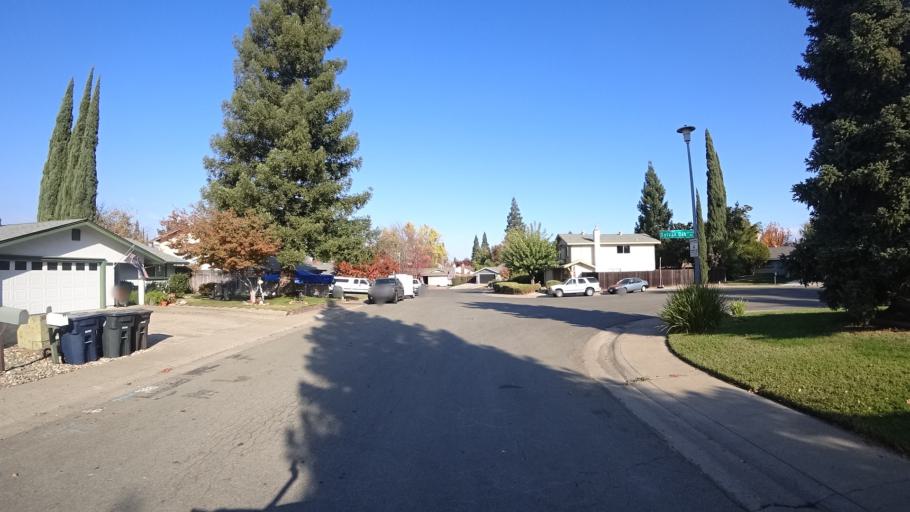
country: US
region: California
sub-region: Sacramento County
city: Citrus Heights
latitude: 38.7104
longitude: -121.2611
